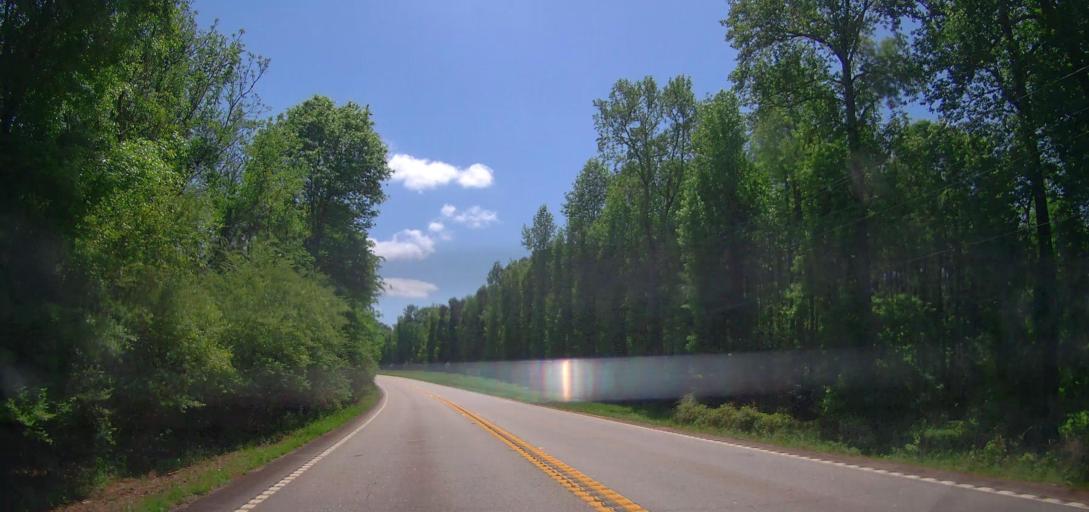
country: US
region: Georgia
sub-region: Jasper County
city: Monticello
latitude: 33.2000
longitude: -83.6576
